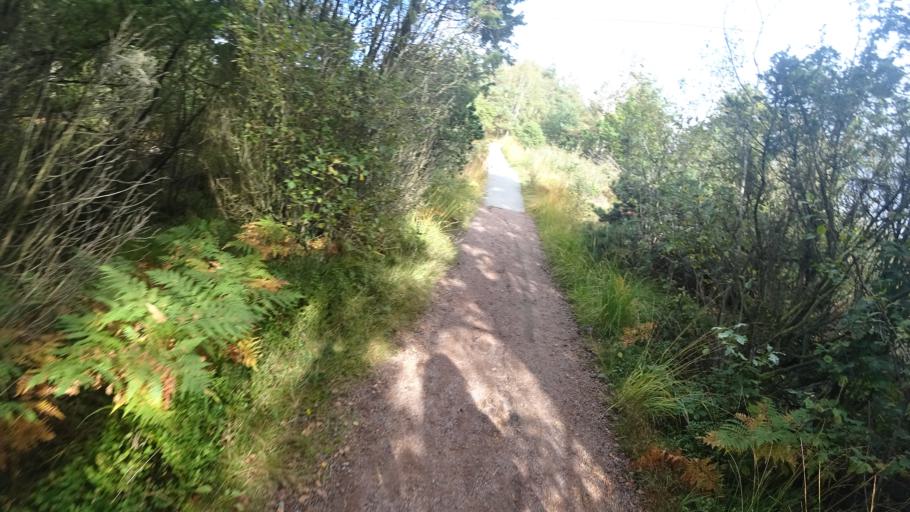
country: SE
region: Vaestra Goetaland
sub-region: Goteborg
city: Billdal
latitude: 57.6046
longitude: 11.9665
